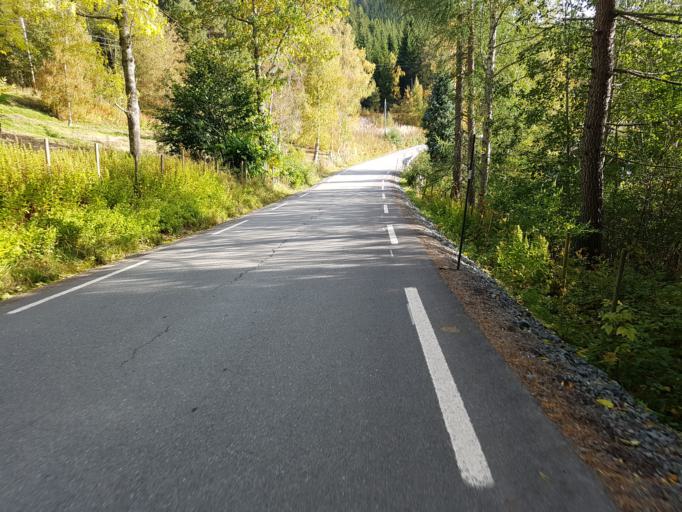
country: NO
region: Sor-Trondelag
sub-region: Malvik
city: Malvik
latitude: 63.3573
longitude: 10.6380
